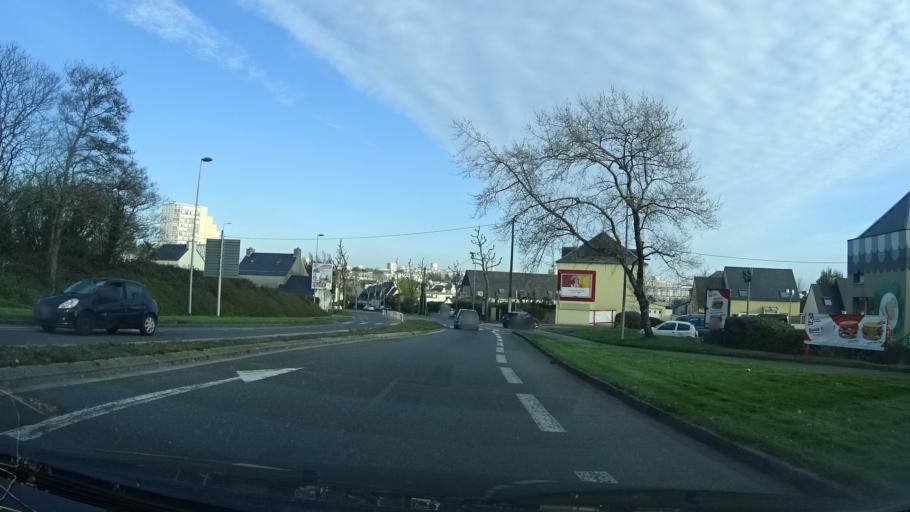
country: FR
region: Brittany
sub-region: Departement du Finistere
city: Brest
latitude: 48.4138
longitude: -4.4787
